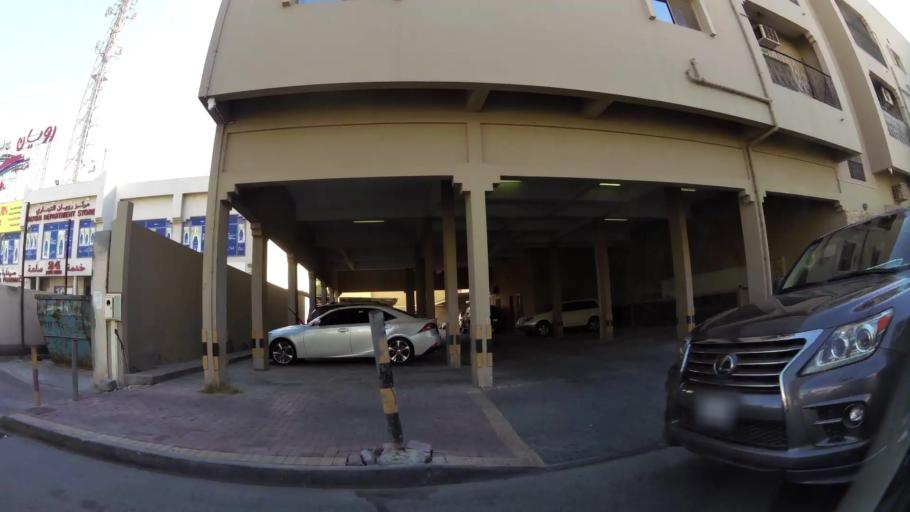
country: BH
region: Muharraq
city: Al Muharraq
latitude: 26.2604
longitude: 50.6083
